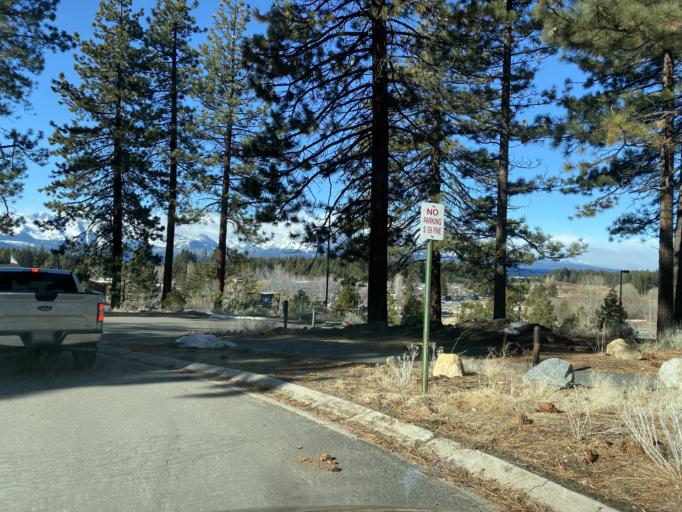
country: US
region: Nevada
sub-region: Douglas County
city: Kingsbury
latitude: 38.9703
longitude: -119.9333
